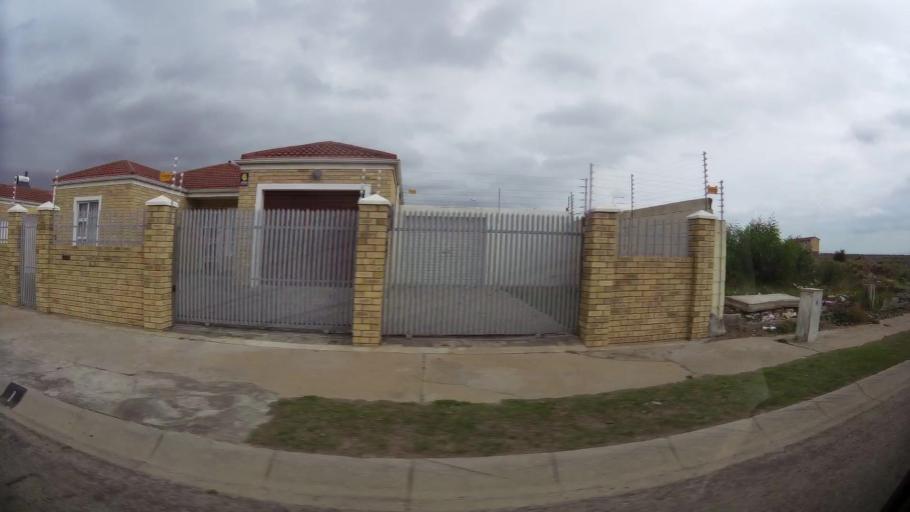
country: ZA
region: Eastern Cape
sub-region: Nelson Mandela Bay Metropolitan Municipality
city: Port Elizabeth
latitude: -33.8922
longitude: 25.5628
